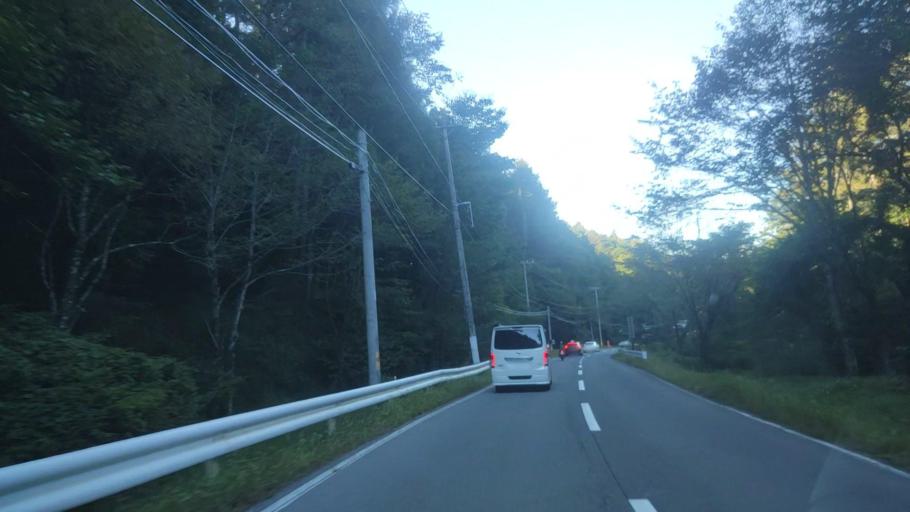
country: JP
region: Nagano
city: Kamimaruko
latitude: 36.2227
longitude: 138.2942
